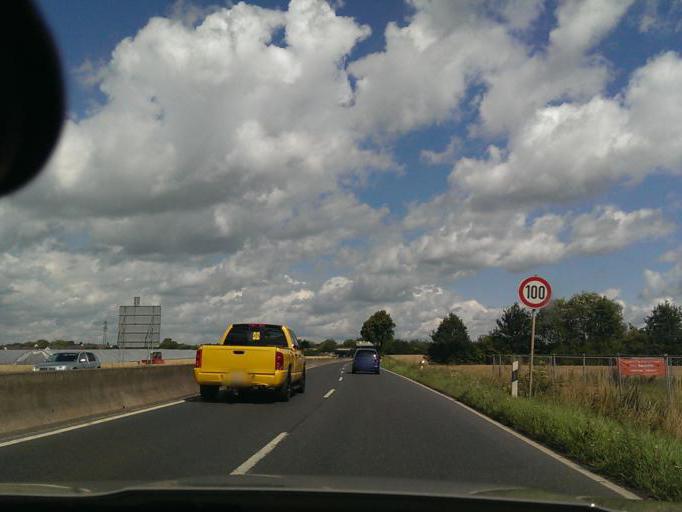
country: DE
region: Lower Saxony
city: Sarstedt
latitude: 52.2750
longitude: 9.8470
